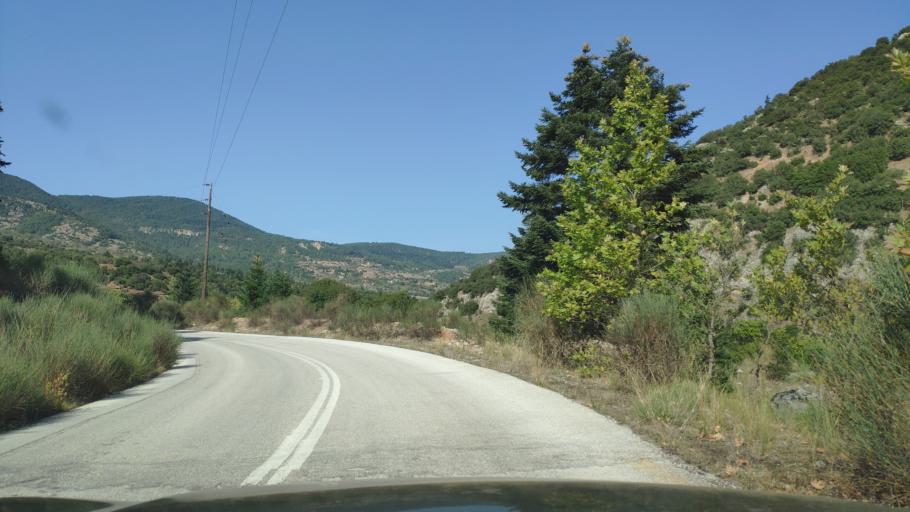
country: GR
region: West Greece
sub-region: Nomos Achaias
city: Aiyira
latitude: 37.9775
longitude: 22.3542
